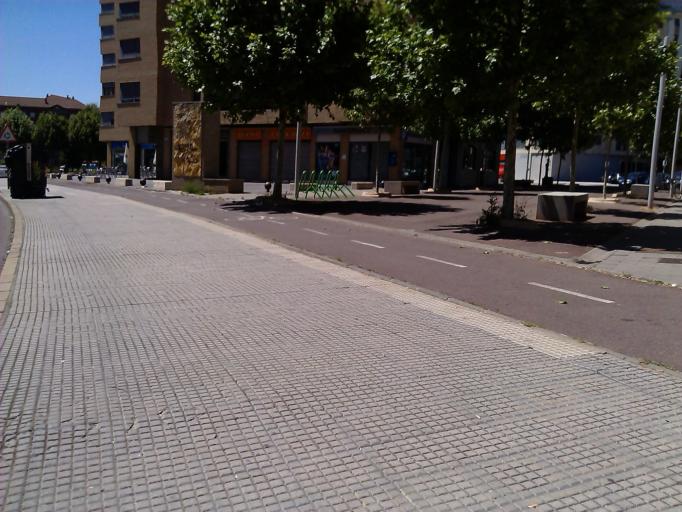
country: ES
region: Castille and Leon
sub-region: Provincia de Leon
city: Leon
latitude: 42.6038
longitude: -5.5614
